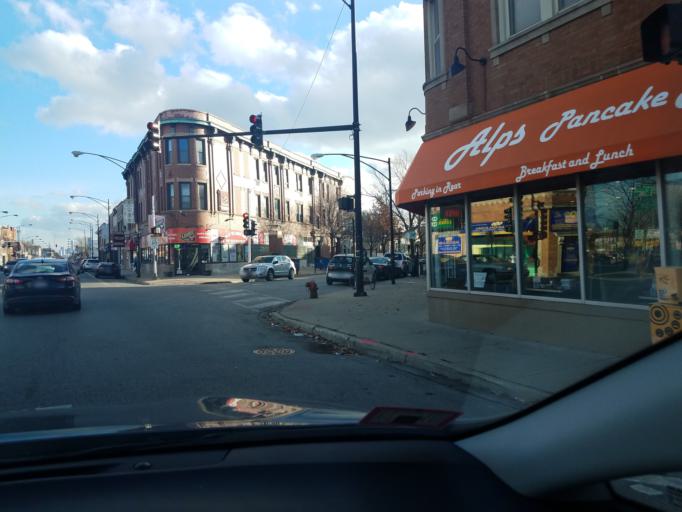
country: US
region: Illinois
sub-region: Cook County
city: Lincolnwood
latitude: 41.9537
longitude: -87.7192
